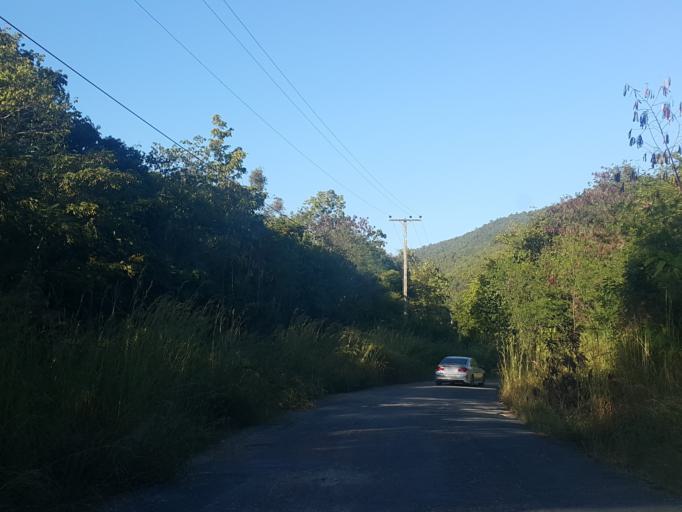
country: TH
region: Chiang Mai
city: San Sai
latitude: 18.9315
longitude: 99.1373
